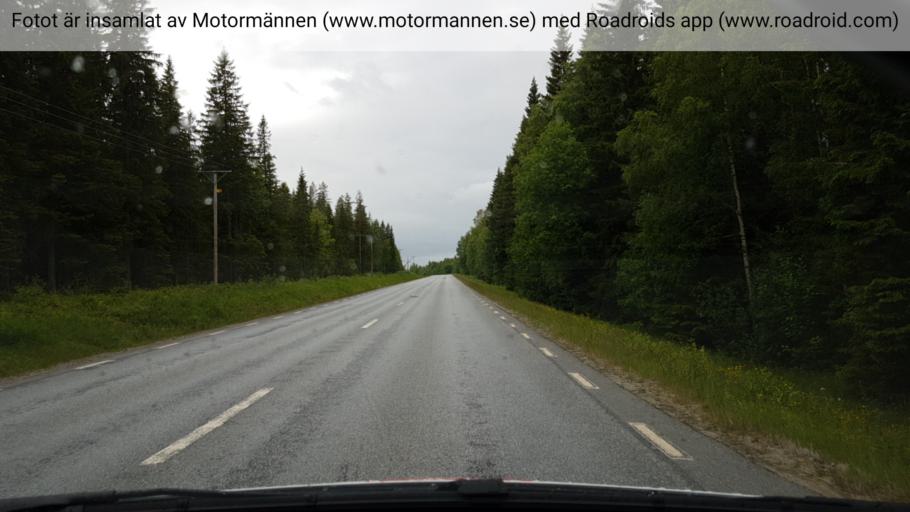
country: SE
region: Vaesterbotten
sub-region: Bjurholms Kommun
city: Bjurholm
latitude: 63.9341
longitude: 19.3380
